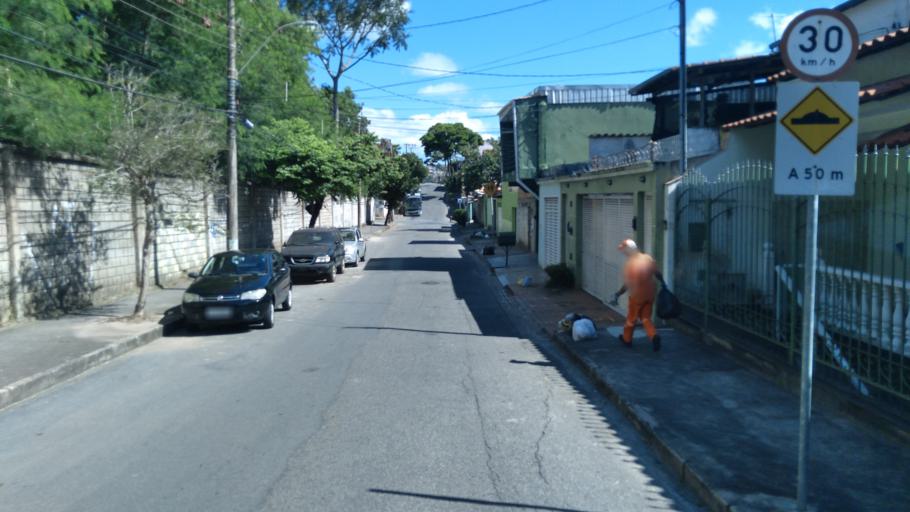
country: BR
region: Minas Gerais
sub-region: Belo Horizonte
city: Belo Horizonte
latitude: -19.8499
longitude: -43.9124
